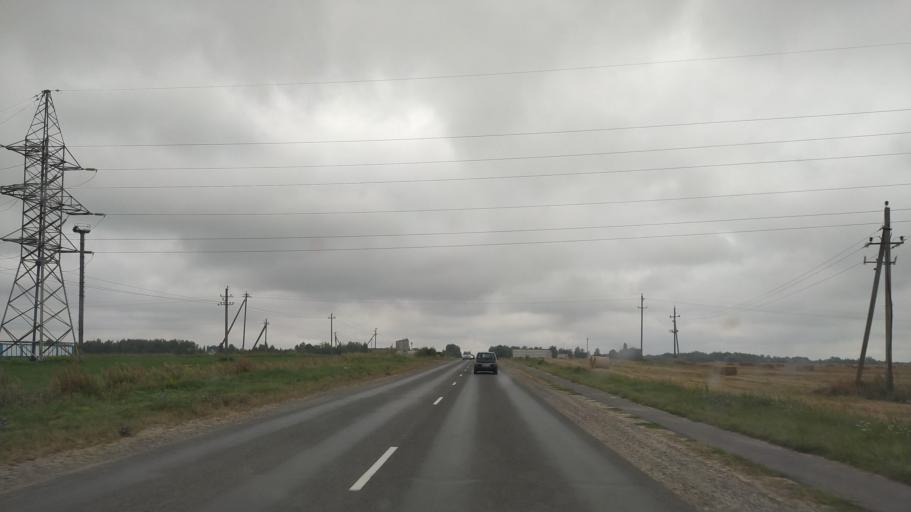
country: BY
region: Brest
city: Byaroza
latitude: 52.5478
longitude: 24.9505
